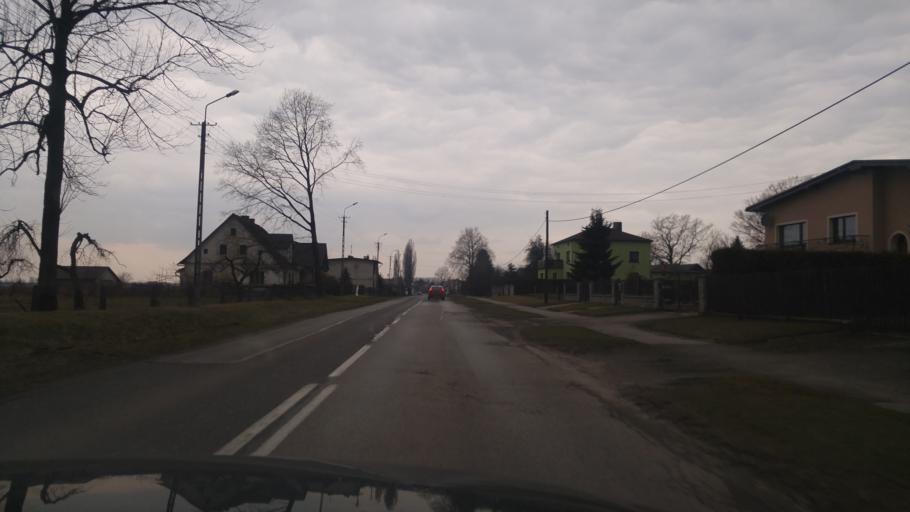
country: PL
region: Silesian Voivodeship
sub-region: Powiat cieszynski
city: Chybie
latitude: 49.9467
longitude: 18.8517
